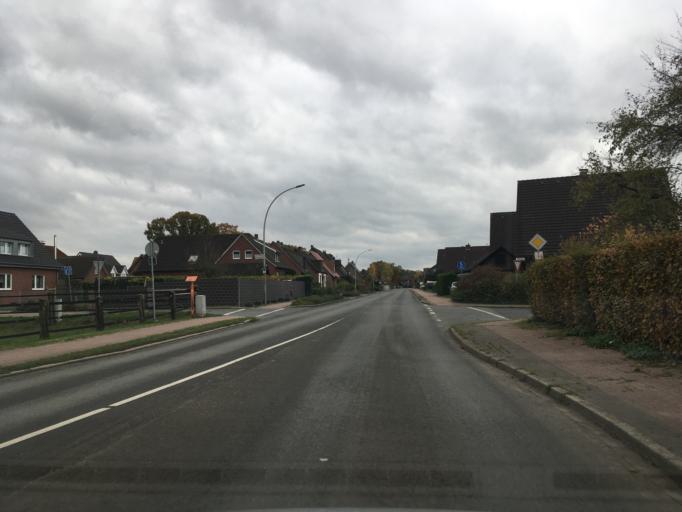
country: DE
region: North Rhine-Westphalia
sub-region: Regierungsbezirk Munster
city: Klein Reken
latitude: 51.8444
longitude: 7.0978
